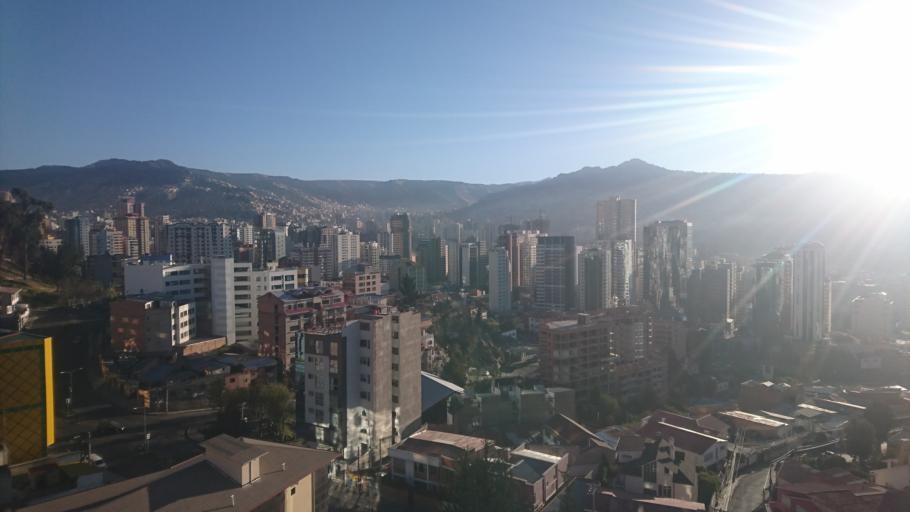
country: BO
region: La Paz
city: La Paz
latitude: -16.5161
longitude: -68.1260
